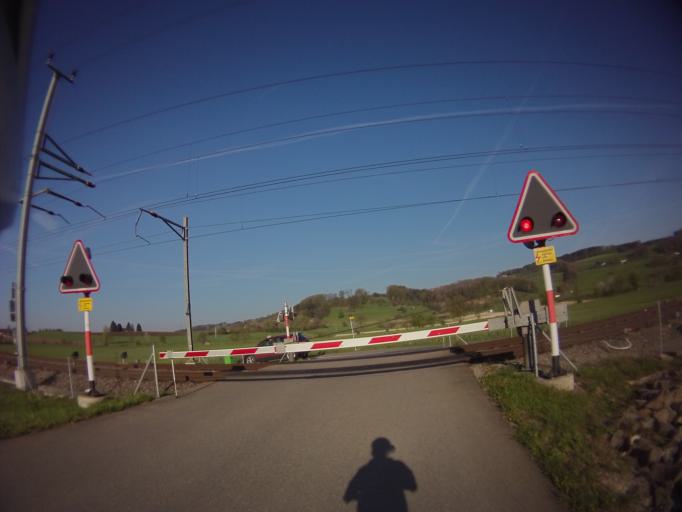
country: CH
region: Zurich
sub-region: Bezirk Affoltern
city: Schachen
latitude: 47.3213
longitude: 8.4676
